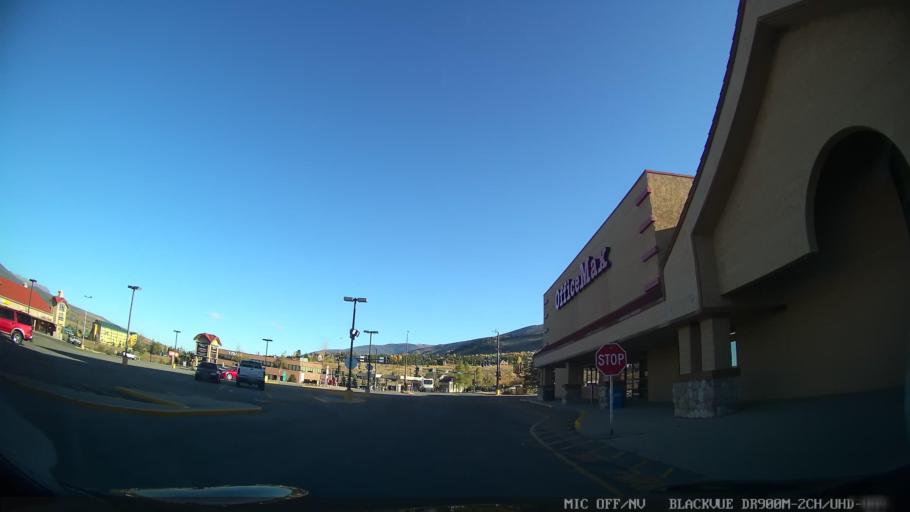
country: US
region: Colorado
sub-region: Summit County
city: Silverthorne
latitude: 39.6272
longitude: -106.0625
